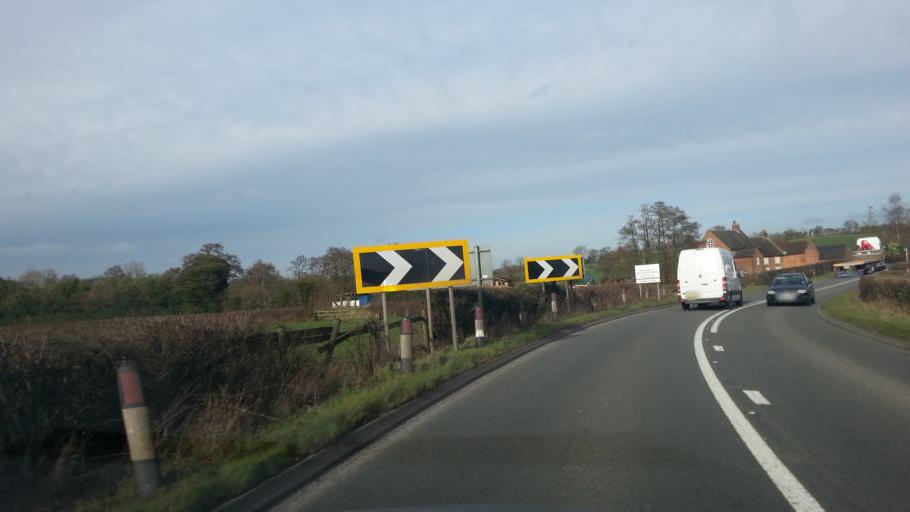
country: GB
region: England
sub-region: Staffordshire
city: Uttoxeter
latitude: 52.8768
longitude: -1.9373
